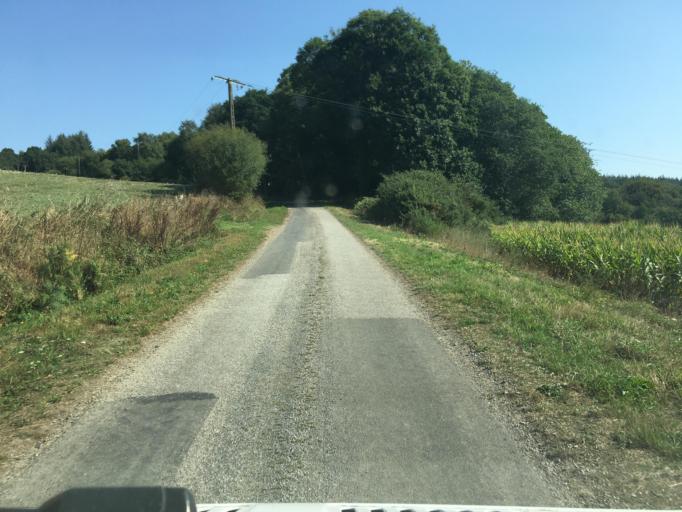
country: FR
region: Brittany
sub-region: Departement des Cotes-d'Armor
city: Mur-de-Bretagne
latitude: 48.2195
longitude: -3.0161
